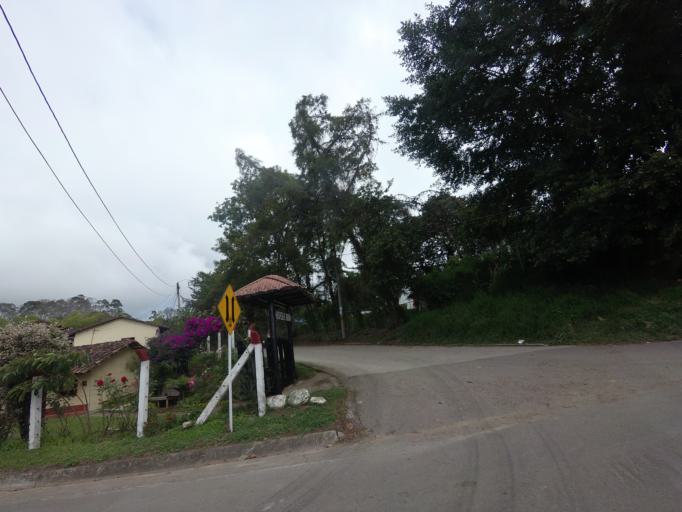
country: CO
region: Huila
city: San Agustin
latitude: 1.8872
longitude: -76.2796
